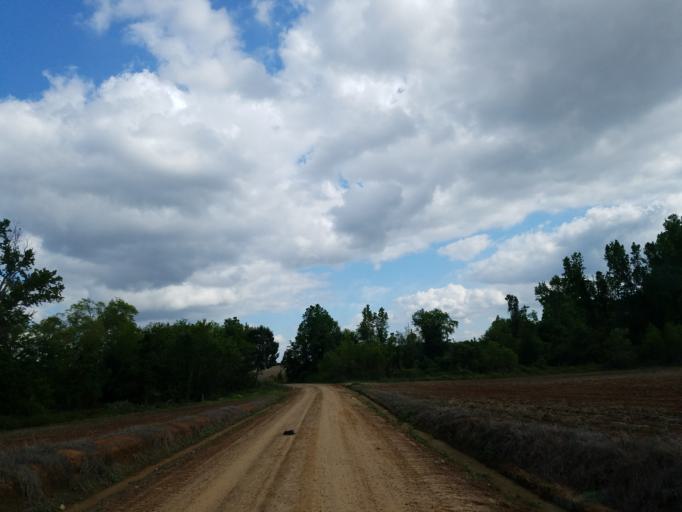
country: US
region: Georgia
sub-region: Dooly County
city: Vienna
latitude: 32.1775
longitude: -83.7812
